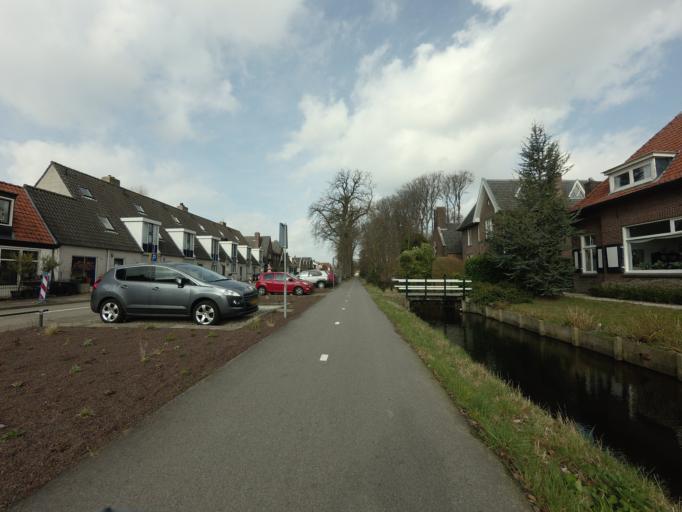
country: NL
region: North Holland
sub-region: Gemeente Wijdemeren
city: Kortenhoef
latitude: 52.2335
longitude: 5.1221
